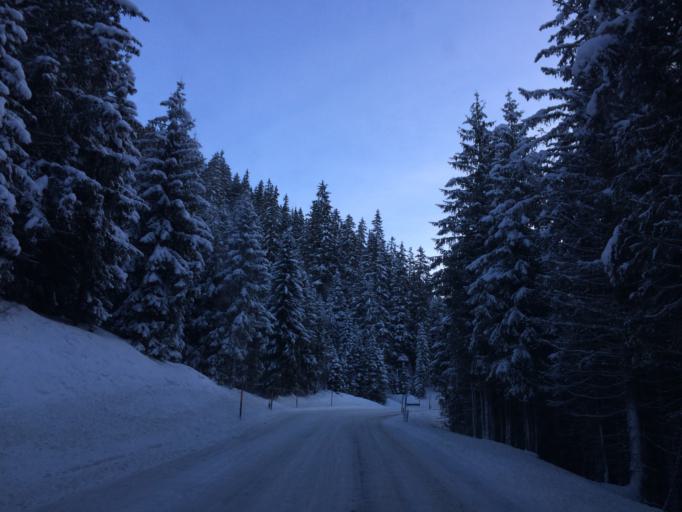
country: CH
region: Grisons
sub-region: Praettigau/Davos District
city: Davos
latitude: 46.8083
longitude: 9.8678
